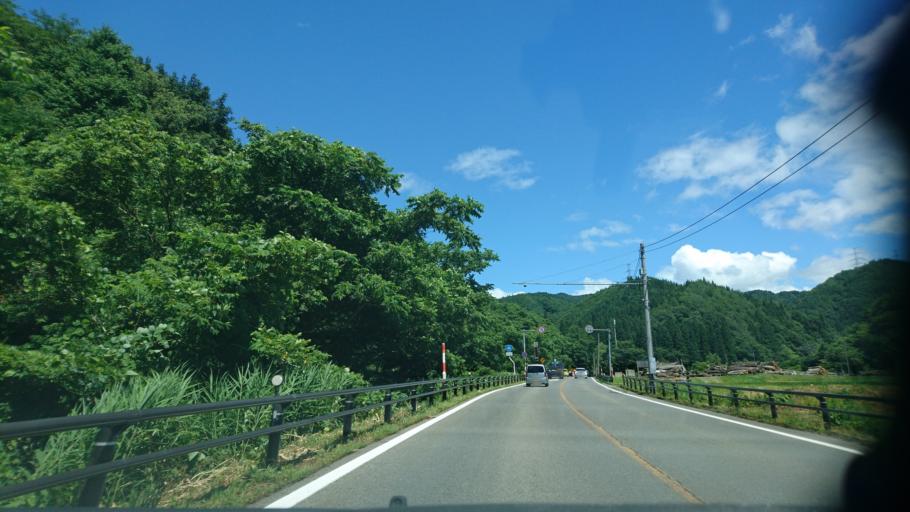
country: JP
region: Akita
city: Kakunodatemachi
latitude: 39.6574
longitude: 140.6719
